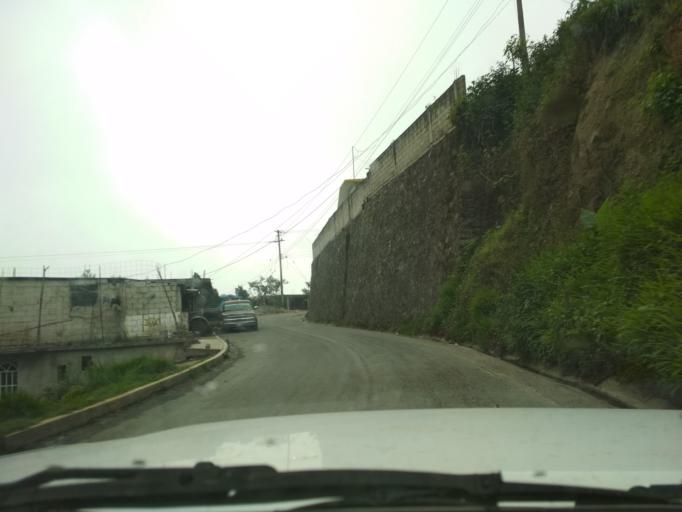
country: MX
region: Veracruz
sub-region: La Perla
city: Metlac Hernandez (Metlac Primero)
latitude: 18.9541
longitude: -97.1748
